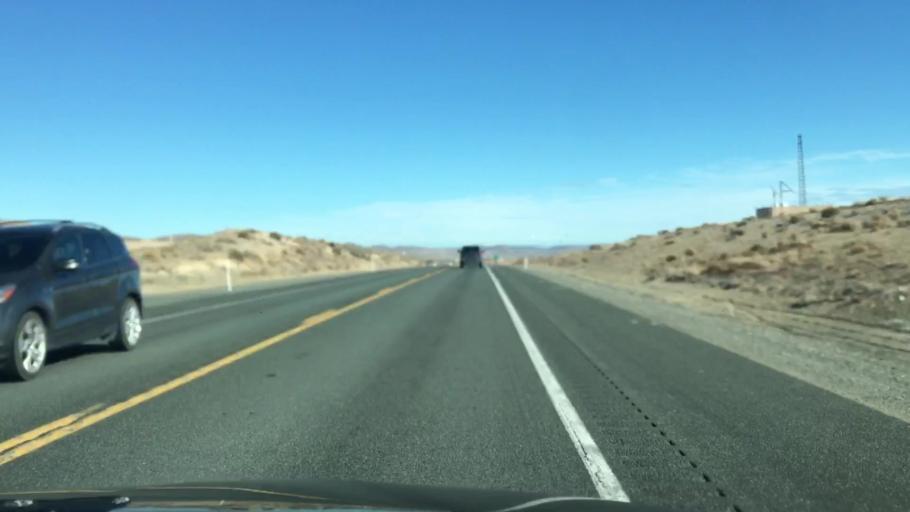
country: US
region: Nevada
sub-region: Lyon County
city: Stagecoach
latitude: 39.3809
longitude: -119.3214
